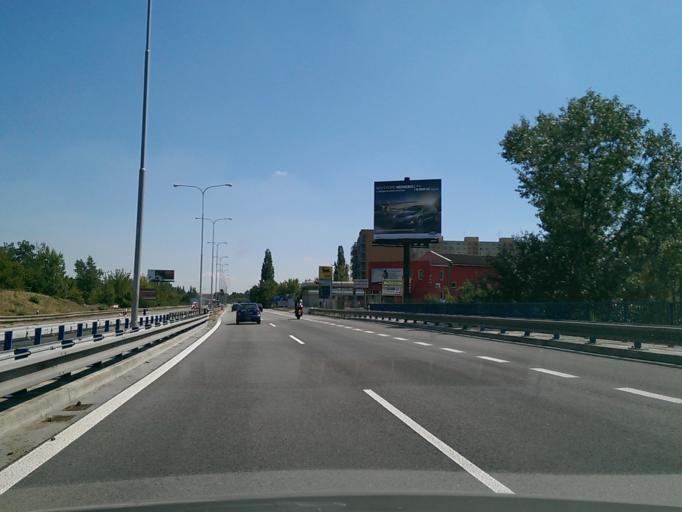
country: CZ
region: South Moravian
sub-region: Mesto Brno
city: Mokra Hora
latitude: 49.2357
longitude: 16.5906
